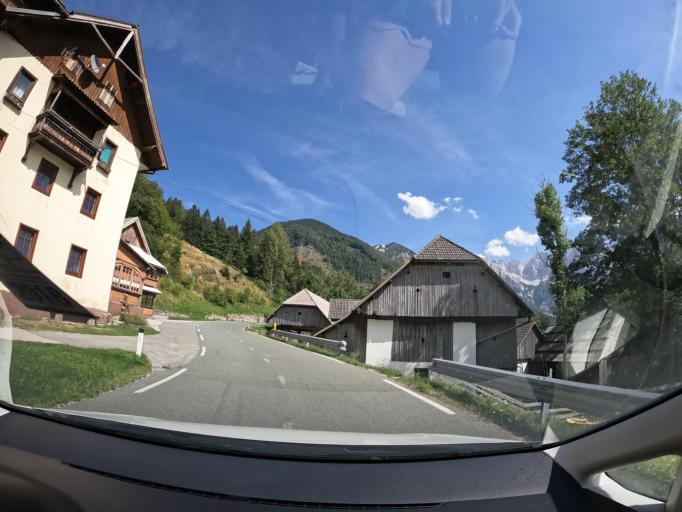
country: AT
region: Carinthia
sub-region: Politischer Bezirk Feldkirchen
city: Glanegg
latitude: 46.7394
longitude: 14.1837
